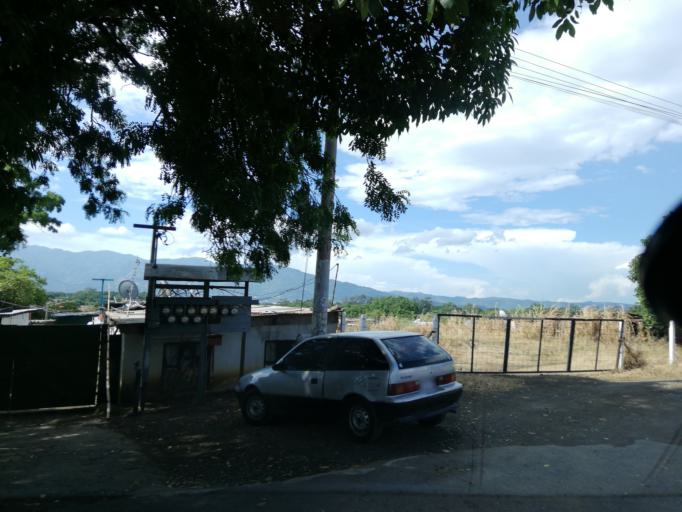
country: CR
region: Heredia
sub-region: Canton de Belen
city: San Antonio
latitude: 9.9917
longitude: -84.2063
